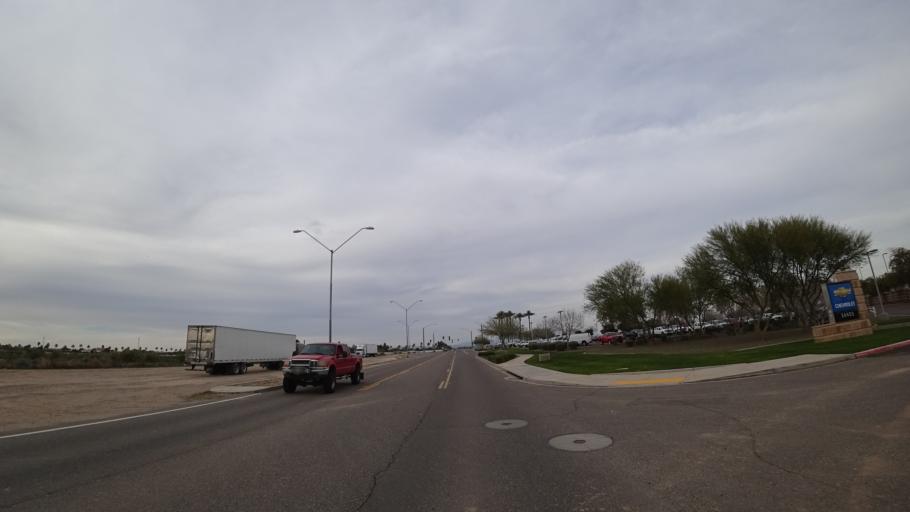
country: US
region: Arizona
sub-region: Maricopa County
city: Citrus Park
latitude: 33.6078
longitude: -112.4267
